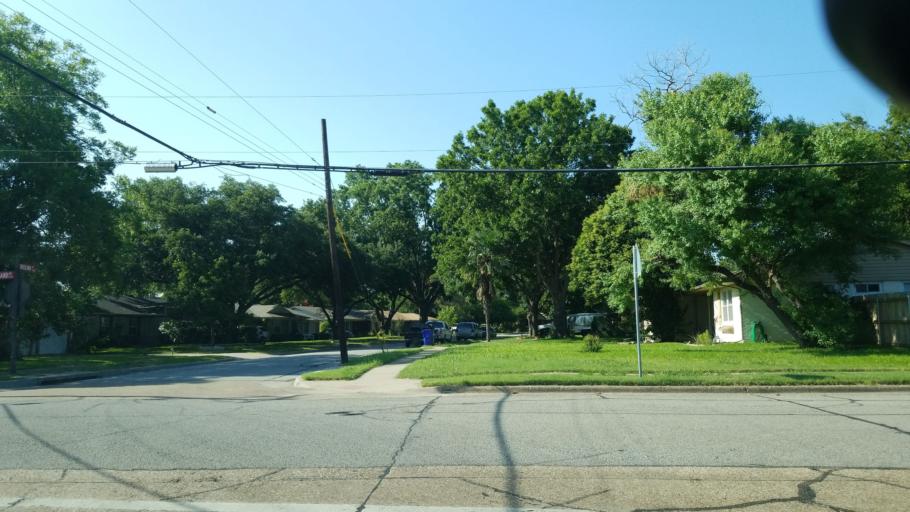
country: US
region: Texas
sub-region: Dallas County
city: Farmers Branch
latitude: 32.9291
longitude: -96.8875
